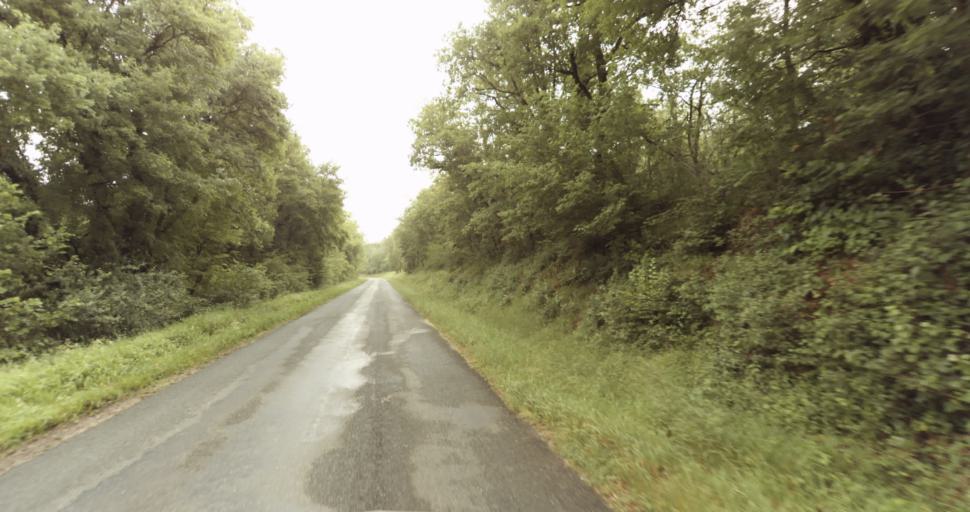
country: FR
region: Aquitaine
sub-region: Departement de la Dordogne
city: Lalinde
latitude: 44.8883
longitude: 0.7729
